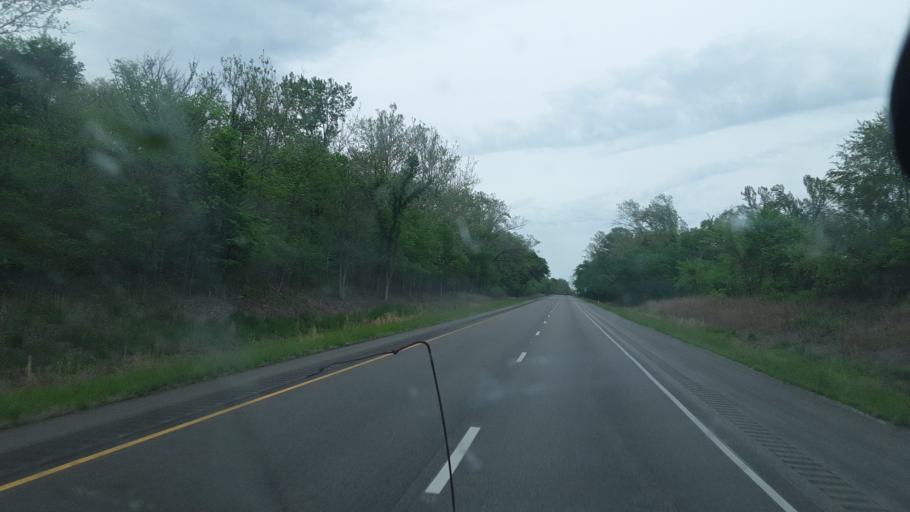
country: US
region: Indiana
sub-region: Posey County
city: Poseyville
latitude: 38.1944
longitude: -87.8504
